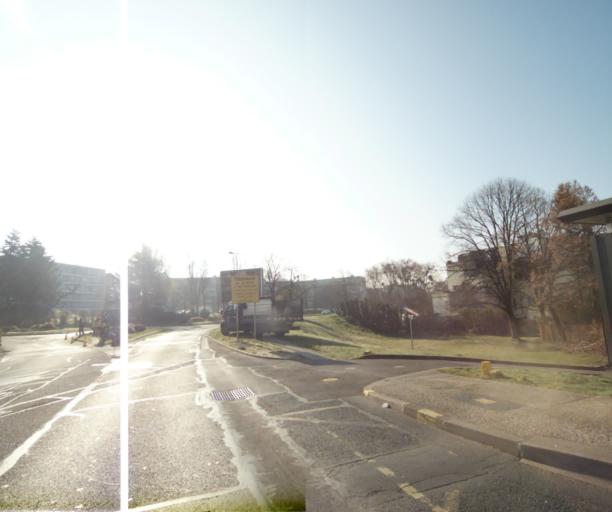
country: FR
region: Ile-de-France
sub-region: Departement du Val-d'Oise
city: Cergy
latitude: 49.0423
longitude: 2.0683
